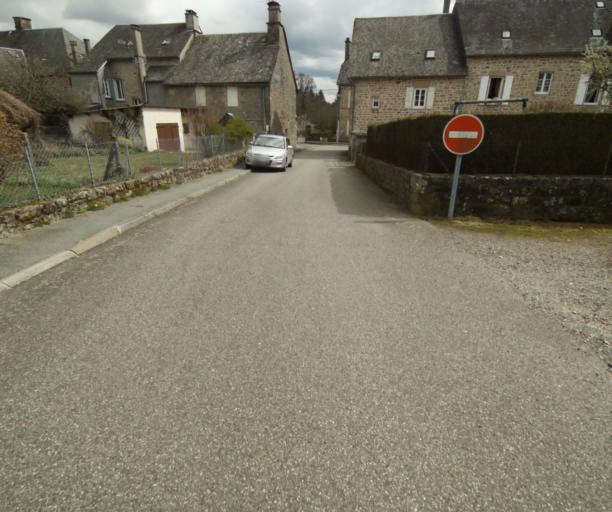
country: FR
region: Limousin
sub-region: Departement de la Correze
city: Correze
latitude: 45.2789
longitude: 1.9732
